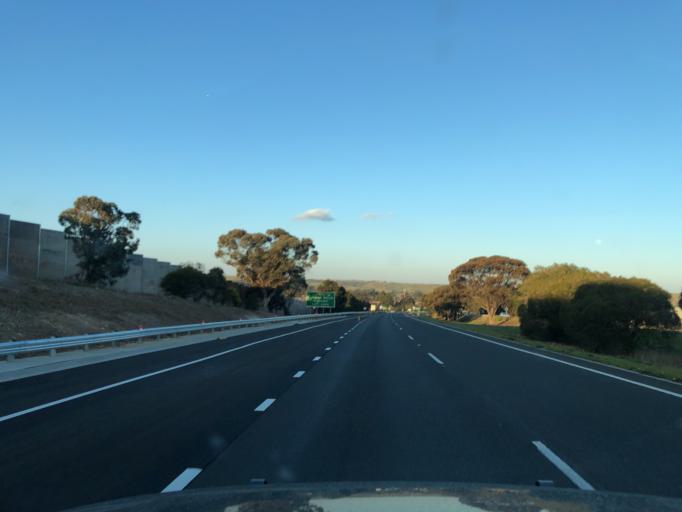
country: AU
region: Victoria
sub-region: Moorabool
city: Bacchus Marsh
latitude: -37.6632
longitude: 144.4287
